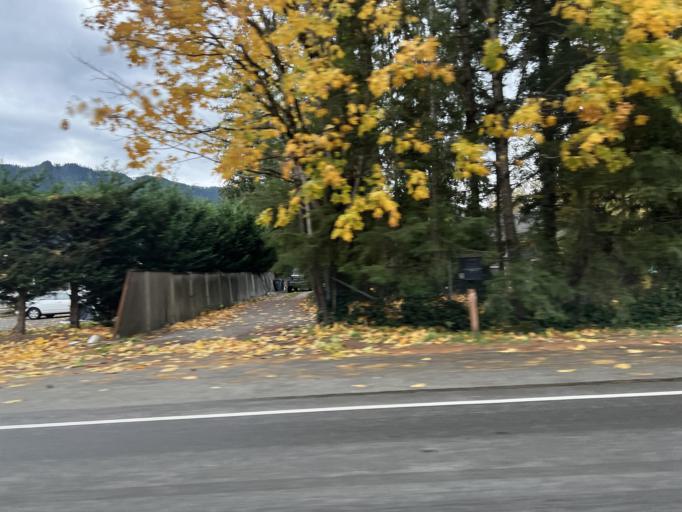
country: US
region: Washington
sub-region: King County
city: Tanner
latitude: 47.4759
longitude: -121.7584
